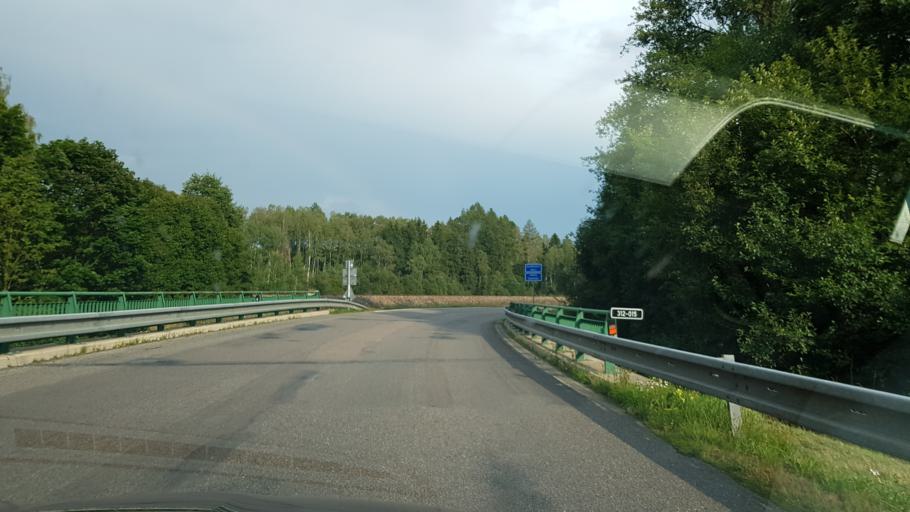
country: CZ
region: Pardubicky
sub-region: Okres Usti nad Orlici
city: Kraliky
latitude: 50.0914
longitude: 16.8151
